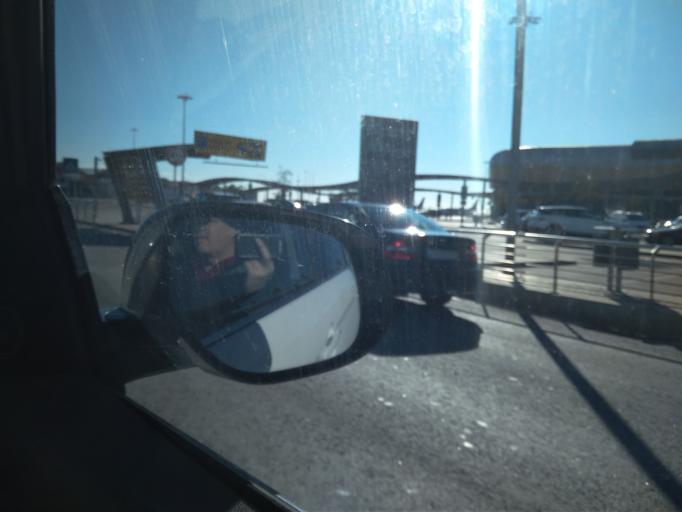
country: PT
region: Faro
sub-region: Faro
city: Faro
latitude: 37.0214
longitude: -7.9671
